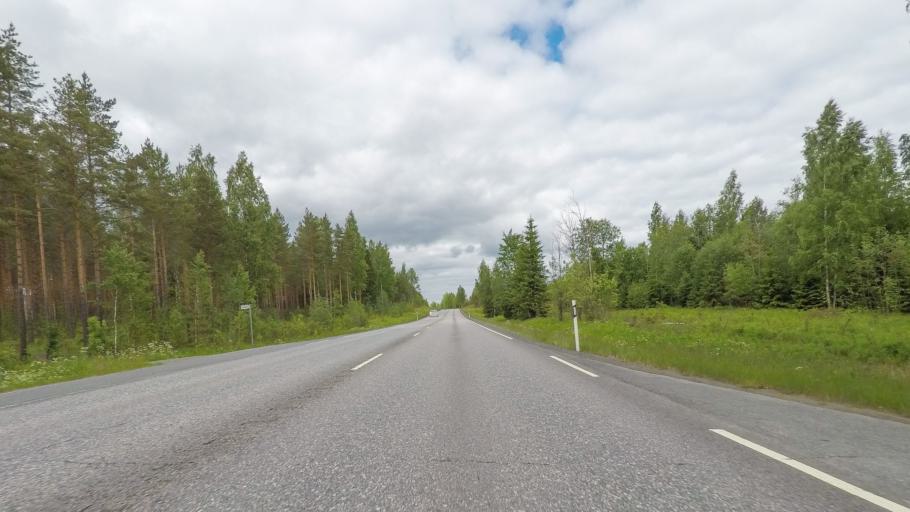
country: FI
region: Central Finland
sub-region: Joutsa
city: Joutsa
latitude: 61.6833
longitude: 26.0550
